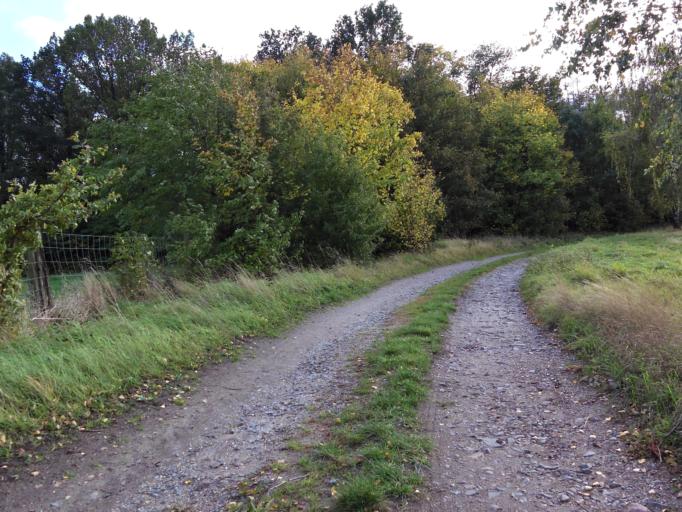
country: DE
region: Saxony
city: Grossposna
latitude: 51.2916
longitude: 12.4921
